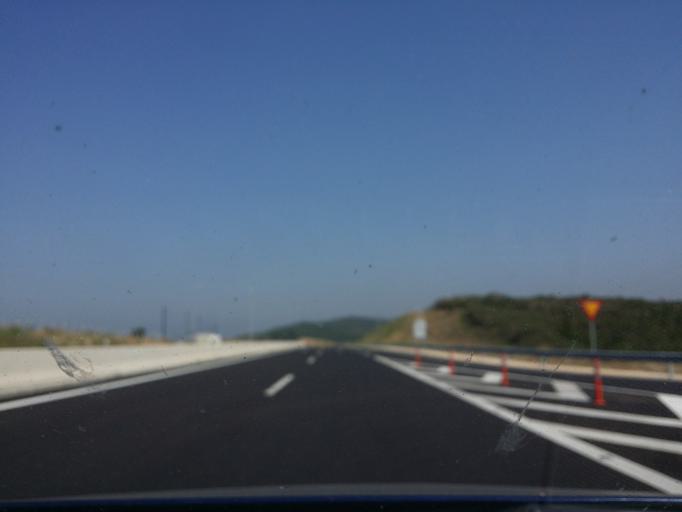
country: GR
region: West Greece
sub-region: Nomos Aitolias kai Akarnanias
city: Menidi
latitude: 39.0249
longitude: 21.1452
